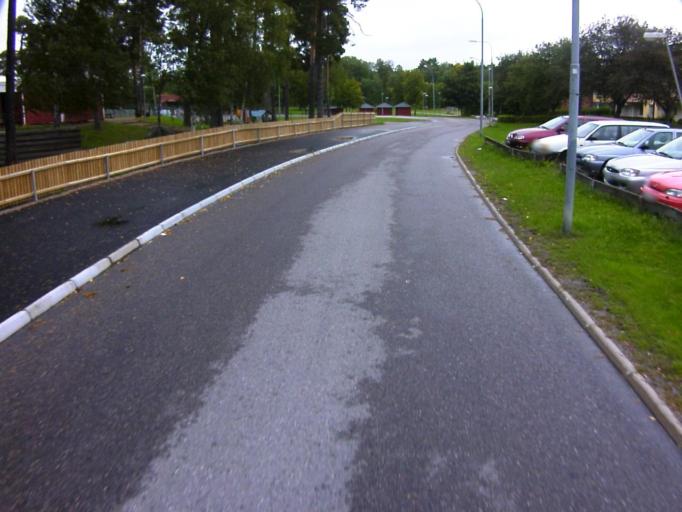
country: SE
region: Soedermanland
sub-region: Eskilstuna Kommun
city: Eskilstuna
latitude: 59.3882
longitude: 16.5411
